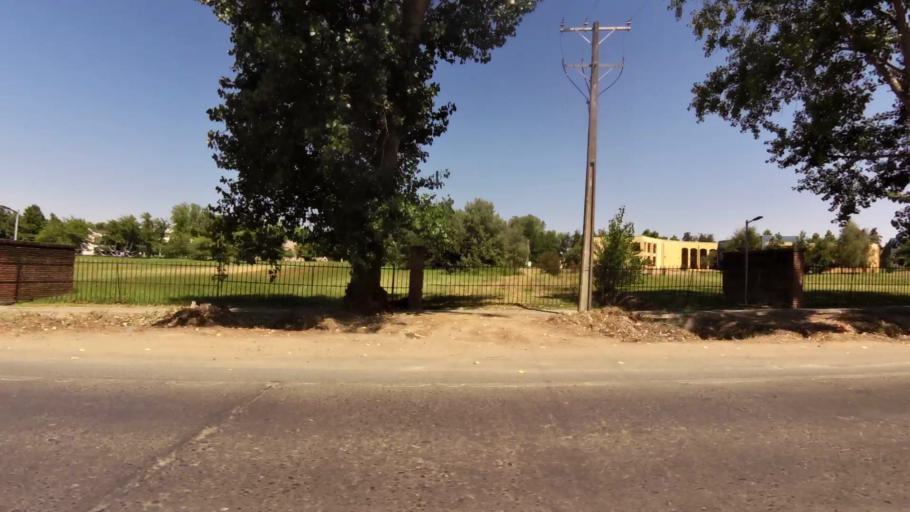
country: CL
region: Maule
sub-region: Provincia de Talca
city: Talca
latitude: -35.4027
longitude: -71.6371
